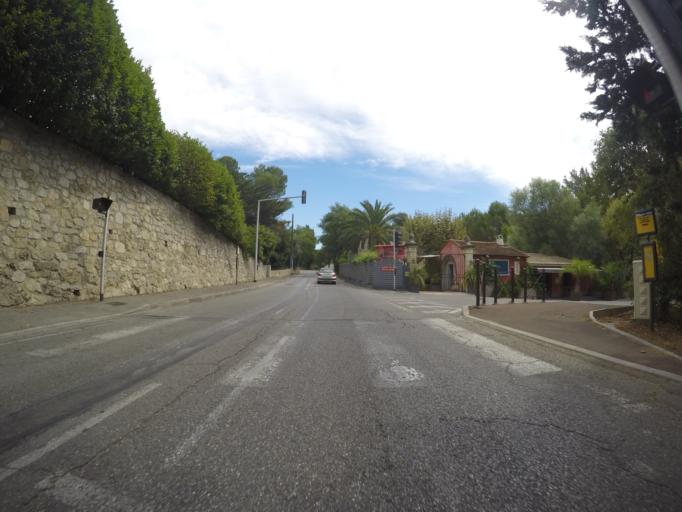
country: FR
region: Provence-Alpes-Cote d'Azur
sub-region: Departement des Alpes-Maritimes
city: Mougins
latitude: 43.6059
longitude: 6.9953
